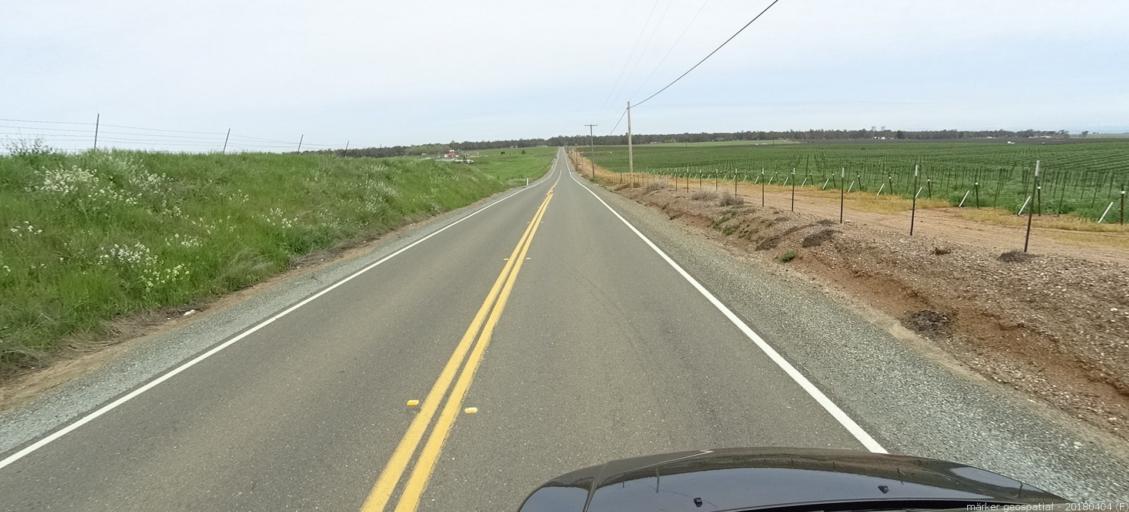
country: US
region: California
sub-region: Sacramento County
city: Clay
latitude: 38.2799
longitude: -121.1713
